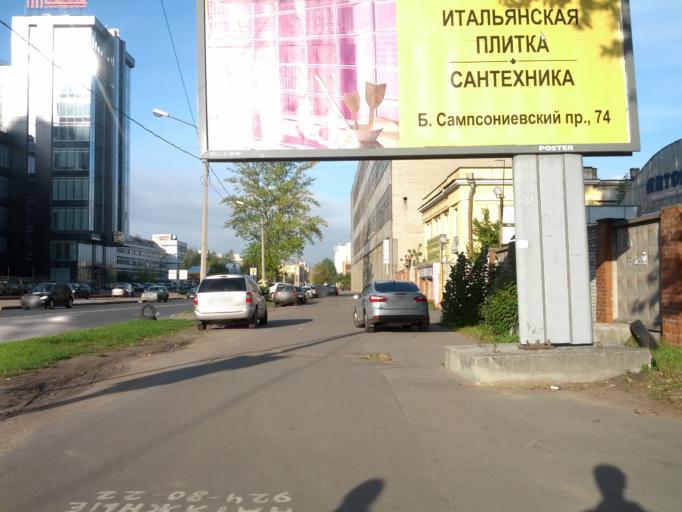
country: RU
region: Leningrad
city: Sampsonievskiy
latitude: 59.9852
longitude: 30.3307
